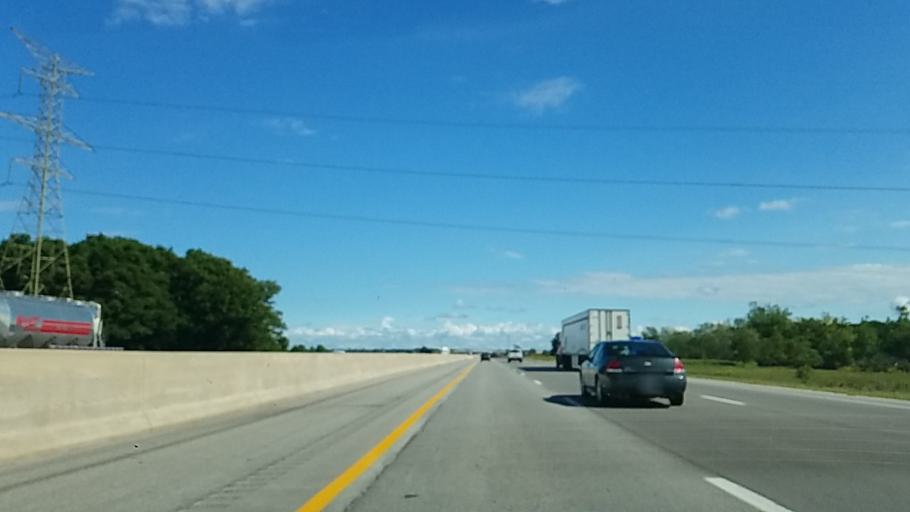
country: US
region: Ohio
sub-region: Ottawa County
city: Genoa
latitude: 41.5080
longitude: -83.4074
